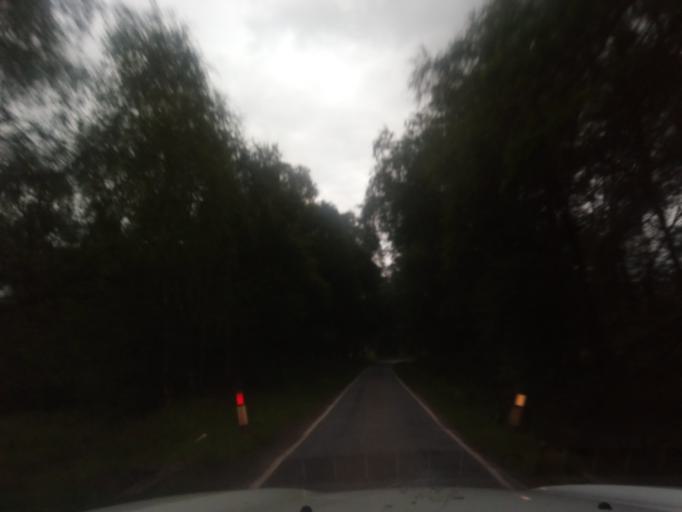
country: GB
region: Scotland
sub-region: Highland
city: Fort William
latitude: 56.8488
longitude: -5.3190
